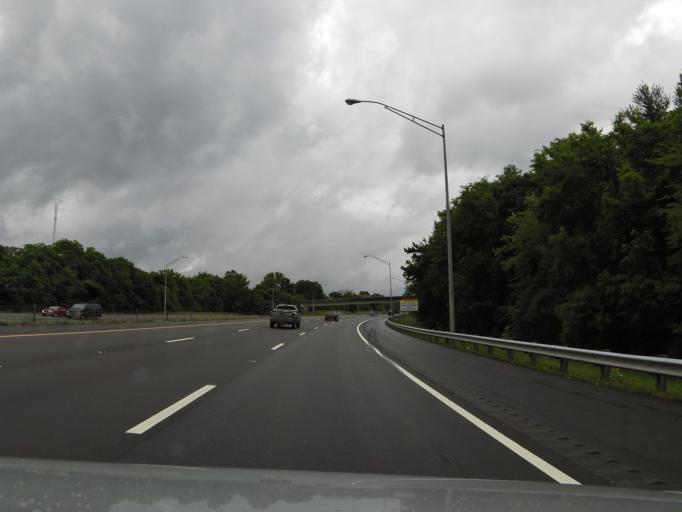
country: US
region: Tennessee
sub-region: Knox County
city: Knoxville
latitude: 35.9822
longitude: -83.9784
